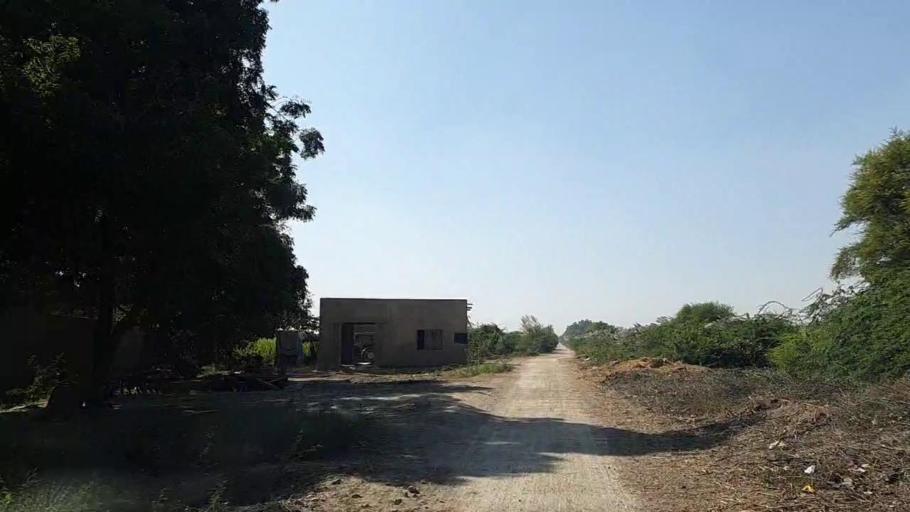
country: PK
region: Sindh
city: Daro Mehar
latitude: 24.8374
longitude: 68.1041
